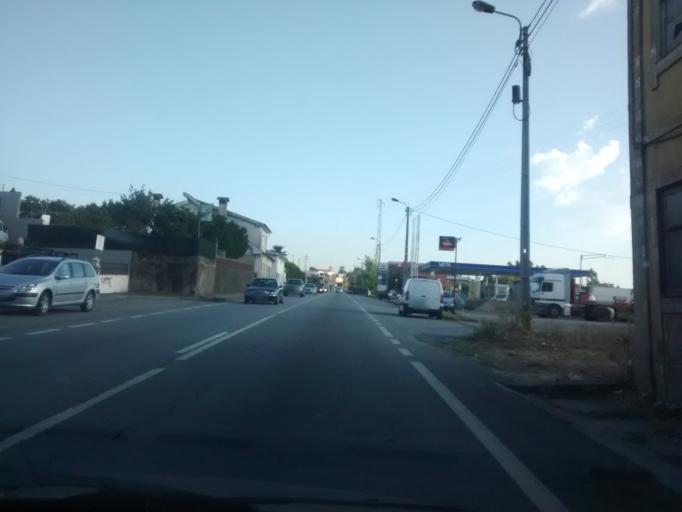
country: PT
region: Braga
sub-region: Braga
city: Adaufe
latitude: 41.5985
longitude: -8.4289
